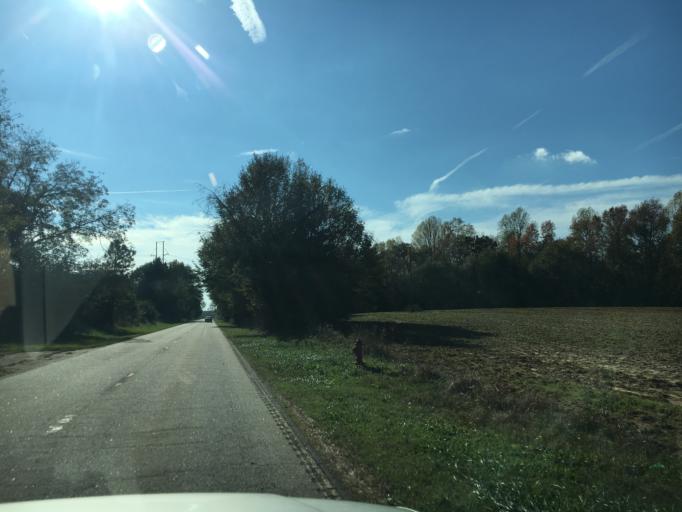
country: US
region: South Carolina
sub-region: Anderson County
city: Iva
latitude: 34.3574
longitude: -82.7247
